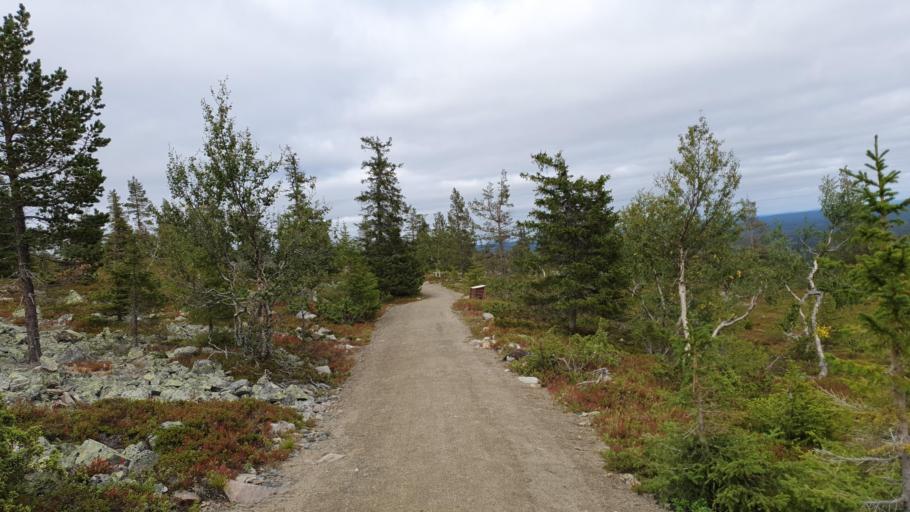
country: FI
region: Lapland
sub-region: Tunturi-Lappi
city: Kolari
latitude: 67.5657
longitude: 24.2604
